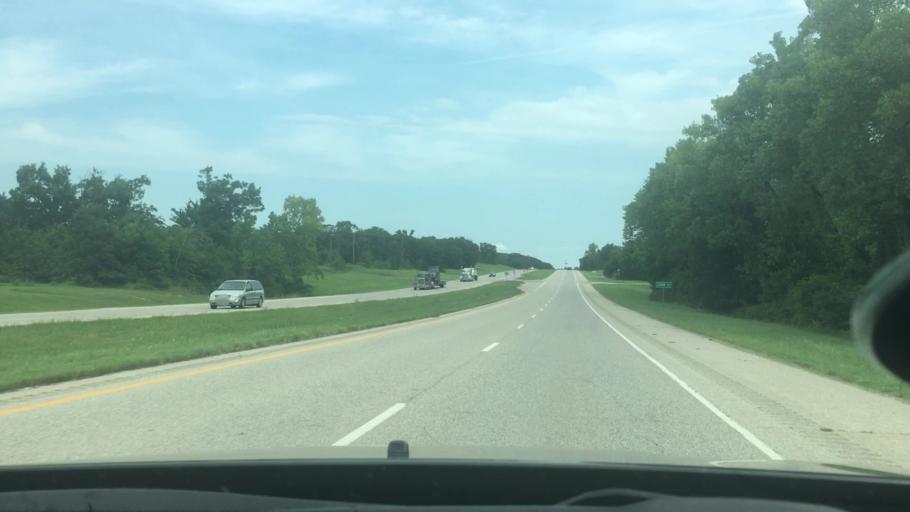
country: US
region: Oklahoma
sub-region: Seminole County
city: Seminole
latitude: 35.2009
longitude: -96.6748
